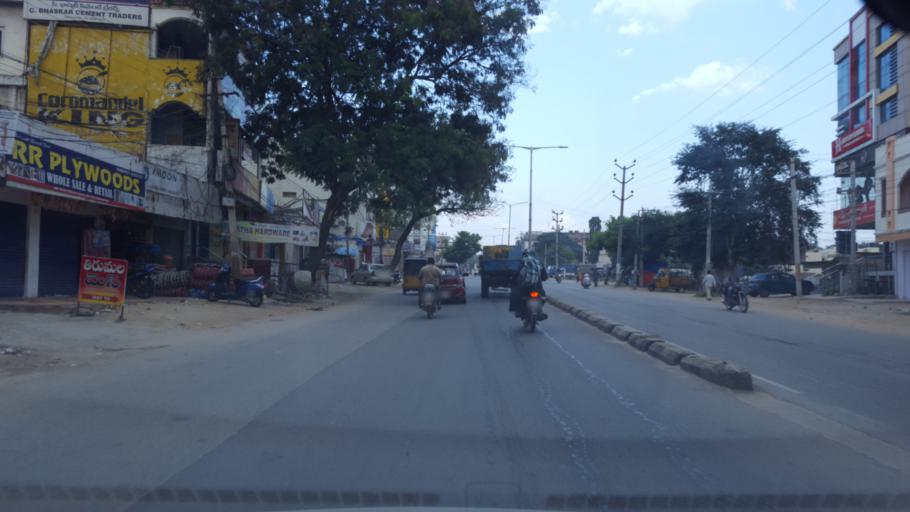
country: IN
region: Telangana
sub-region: Mahbubnagar
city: Mahbubnagar
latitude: 16.7496
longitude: 78.0047
